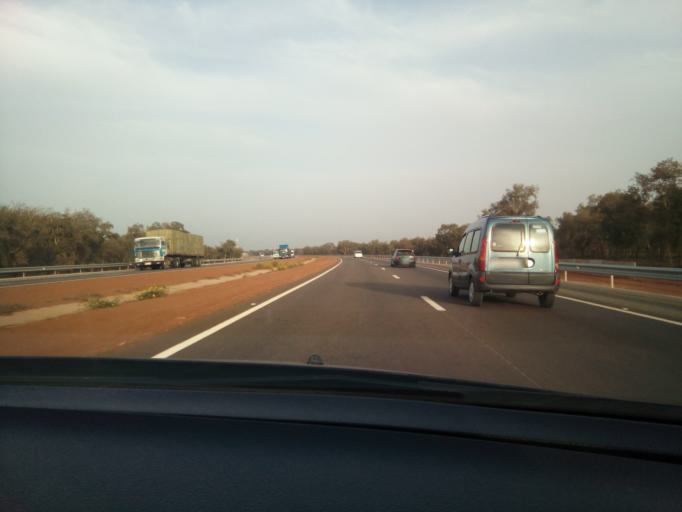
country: MA
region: Rabat-Sale-Zemmour-Zaer
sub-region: Skhirate-Temara
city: Temara
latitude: 33.8381
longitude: -6.8779
